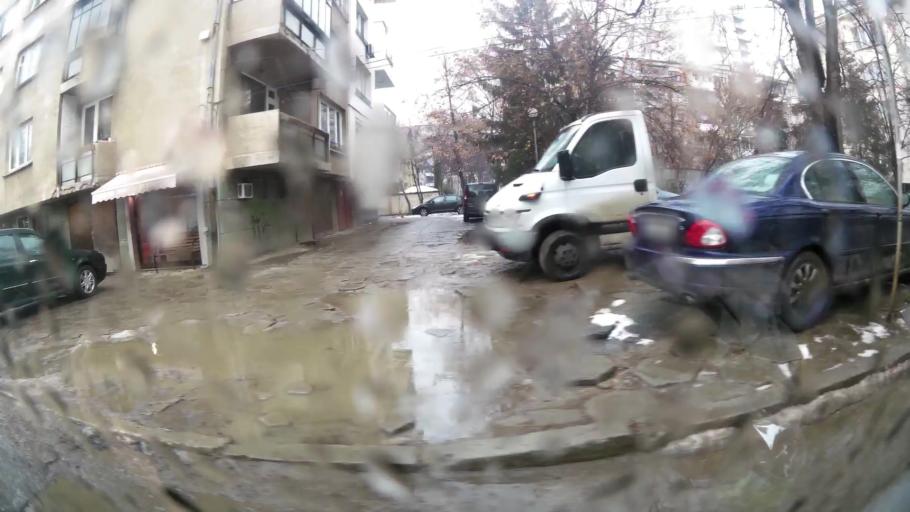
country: BG
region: Sofia-Capital
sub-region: Stolichna Obshtina
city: Sofia
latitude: 42.6742
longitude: 23.3020
